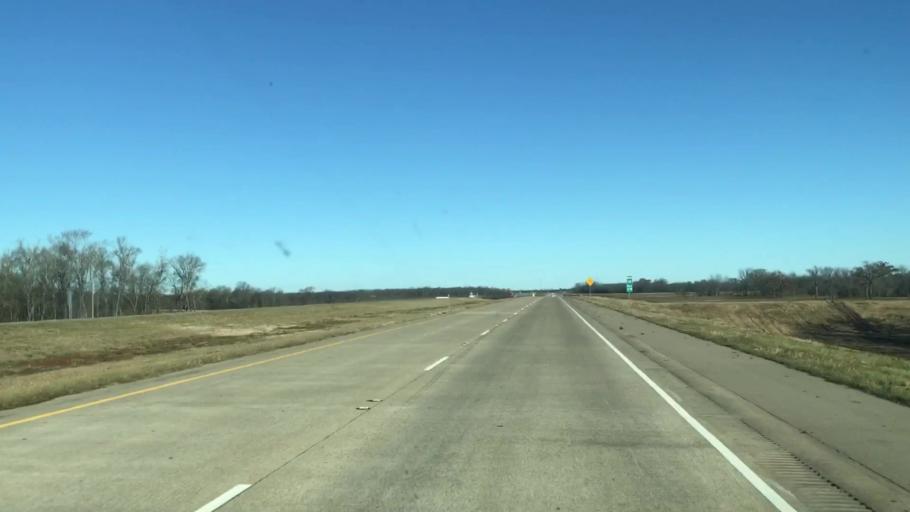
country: US
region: Louisiana
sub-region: Caddo Parish
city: Blanchard
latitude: 32.6279
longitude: -93.8368
